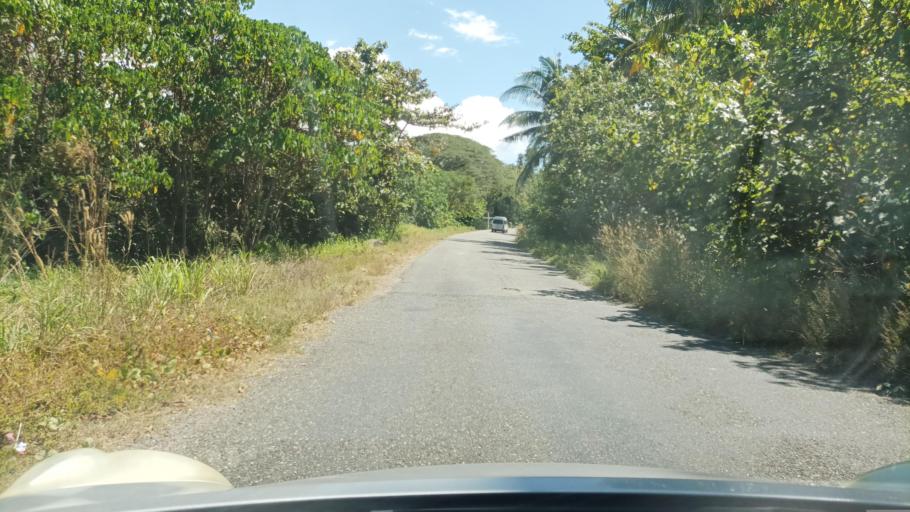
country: SB
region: Guadalcanal
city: Honiara
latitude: -9.3612
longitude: 159.8507
